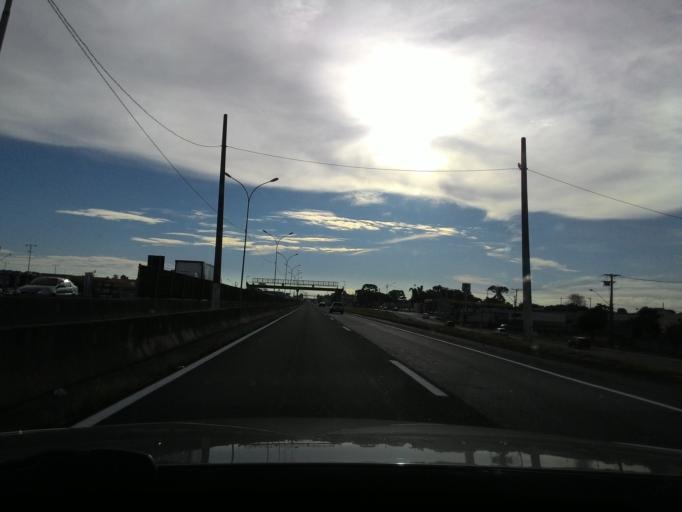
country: BR
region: Parana
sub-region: Quatro Barras
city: Quatro Barras
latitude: -25.3658
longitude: -49.0937
